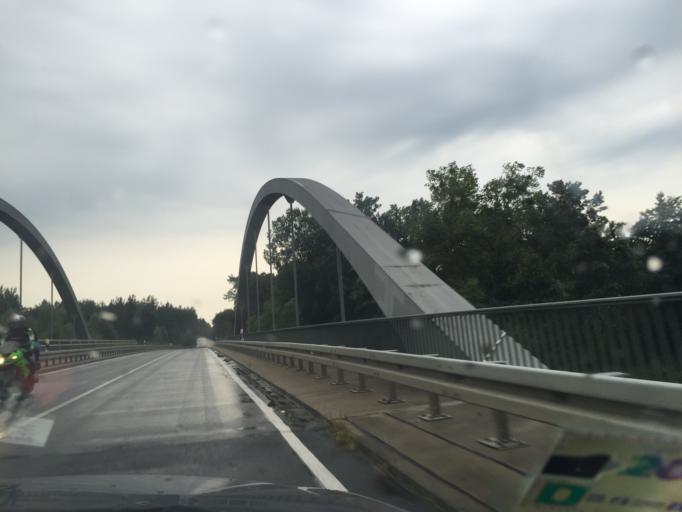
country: DE
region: Brandenburg
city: Liebenwalde
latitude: 52.8416
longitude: 13.4058
